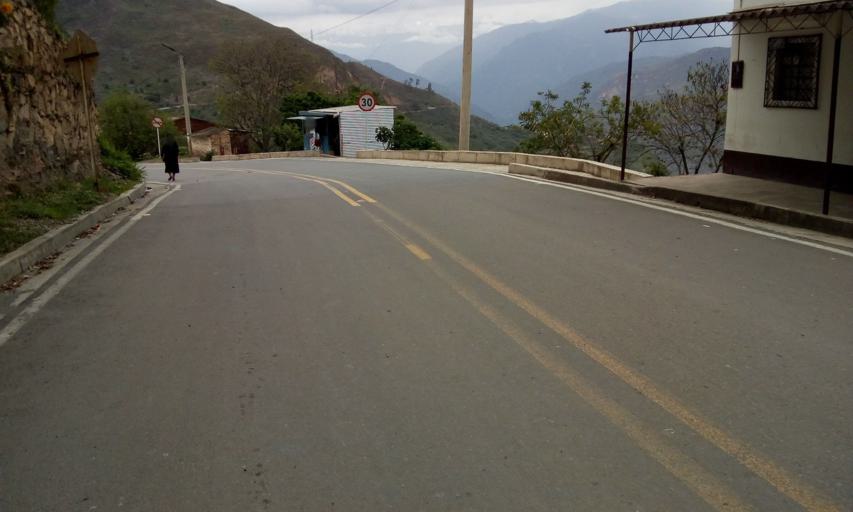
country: CO
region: Boyaca
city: Tipacoque
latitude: 6.4131
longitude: -72.6873
